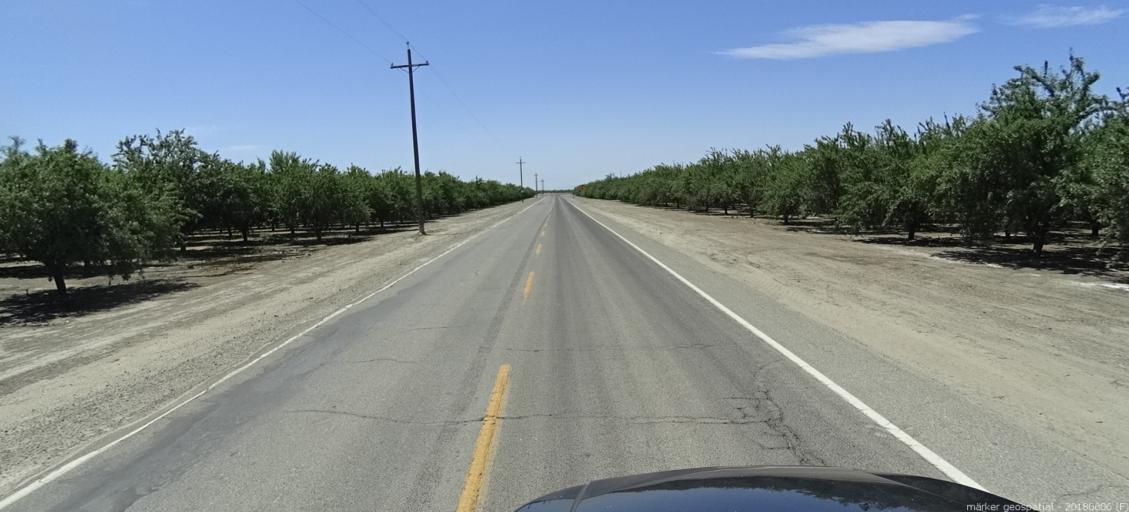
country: US
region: California
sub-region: Fresno County
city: Firebaugh
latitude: 36.8625
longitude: -120.3819
